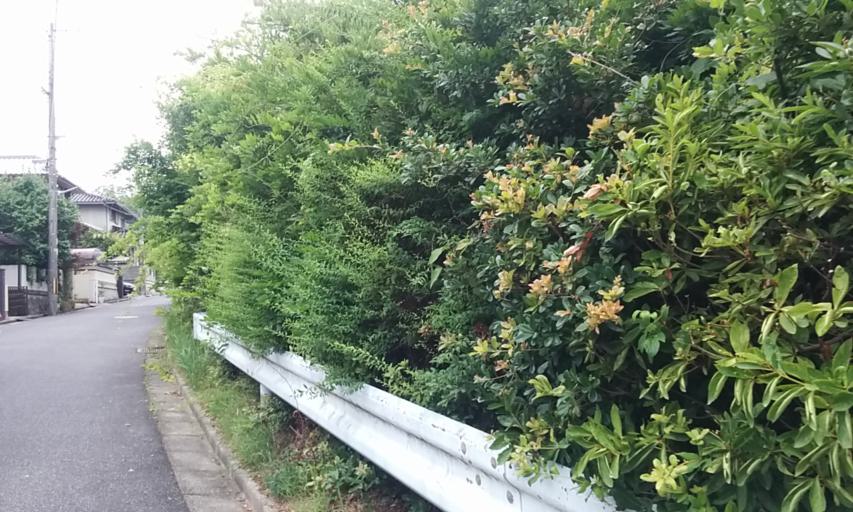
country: JP
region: Kyoto
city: Uji
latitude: 34.8783
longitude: 135.8071
